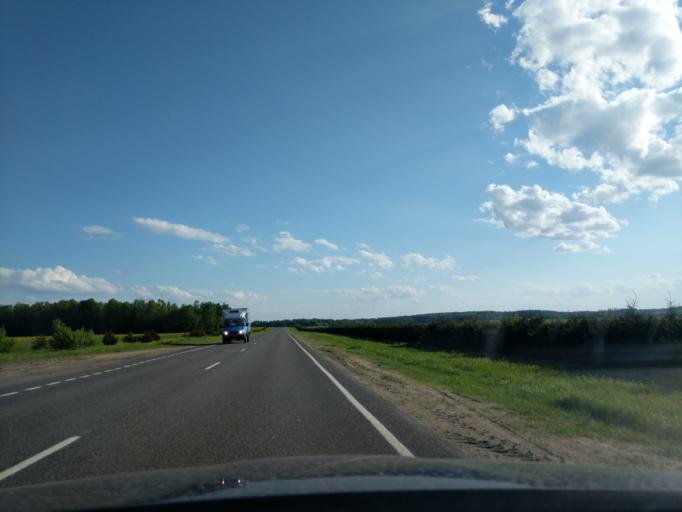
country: BY
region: Minsk
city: Kryvichy
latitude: 54.6482
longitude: 27.1732
